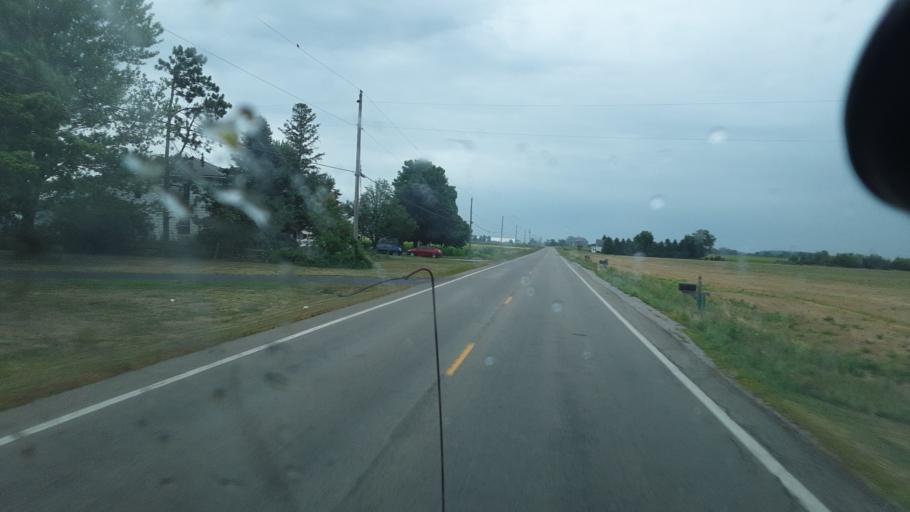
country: US
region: Ohio
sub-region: Defiance County
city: Hicksville
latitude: 41.2962
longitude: -84.7181
